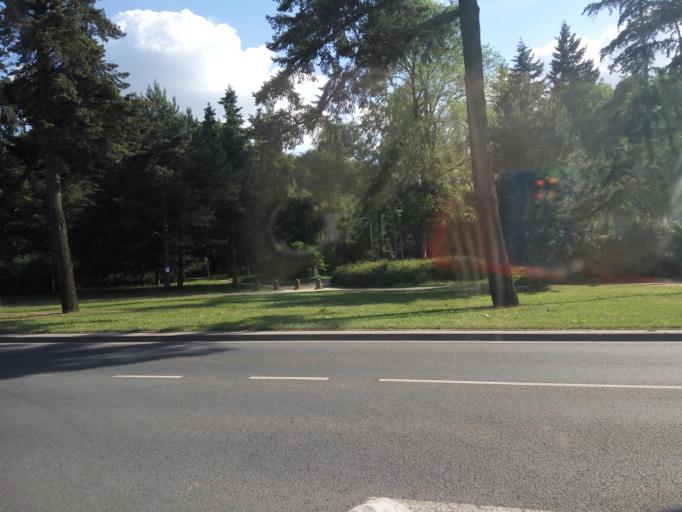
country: PL
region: Lower Silesian Voivodeship
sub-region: Powiat wroclawski
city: Wroclaw
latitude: 51.1325
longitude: 16.9734
